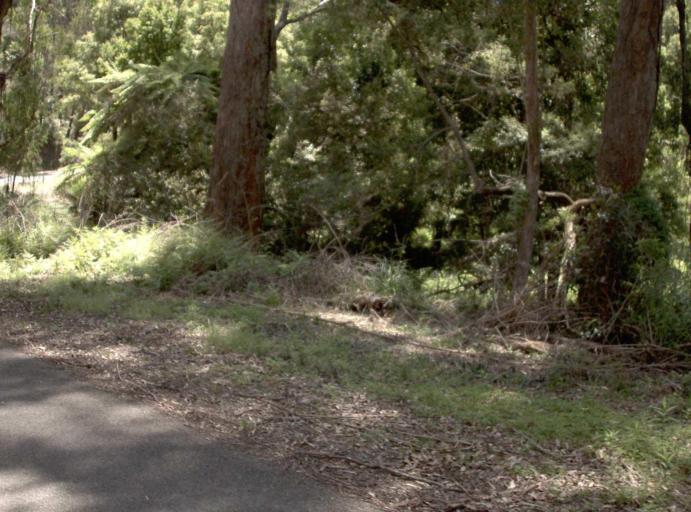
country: AU
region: New South Wales
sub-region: Bombala
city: Bombala
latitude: -37.4767
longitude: 148.9255
